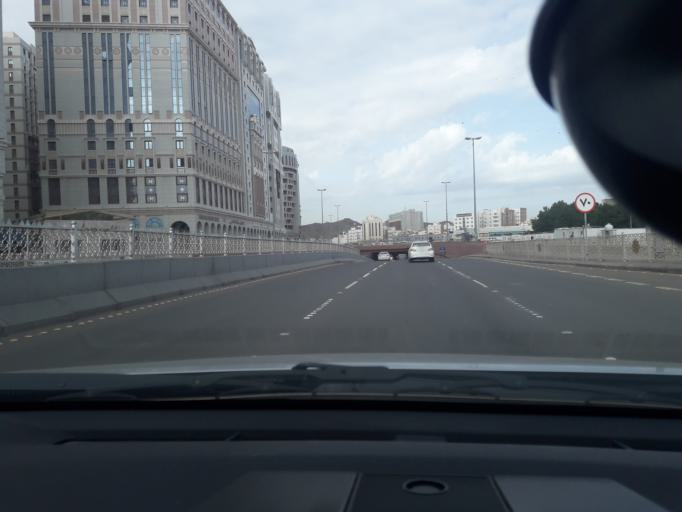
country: SA
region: Al Madinah al Munawwarah
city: Medina
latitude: 24.4737
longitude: 39.6140
